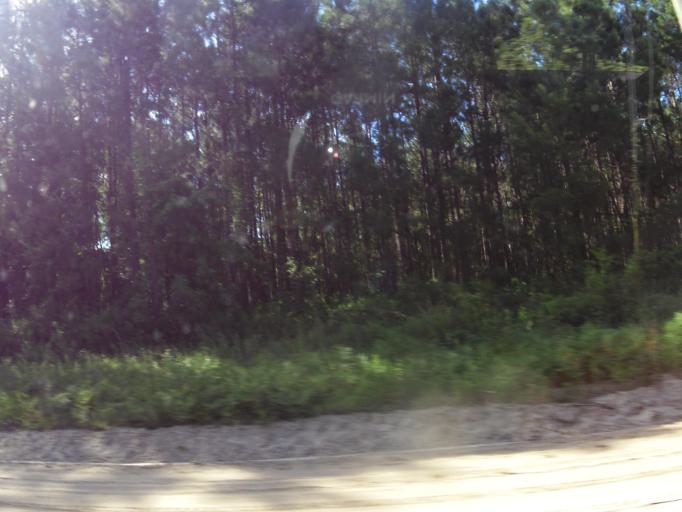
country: US
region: Florida
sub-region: Nassau County
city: Callahan
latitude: 30.5673
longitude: -81.7832
